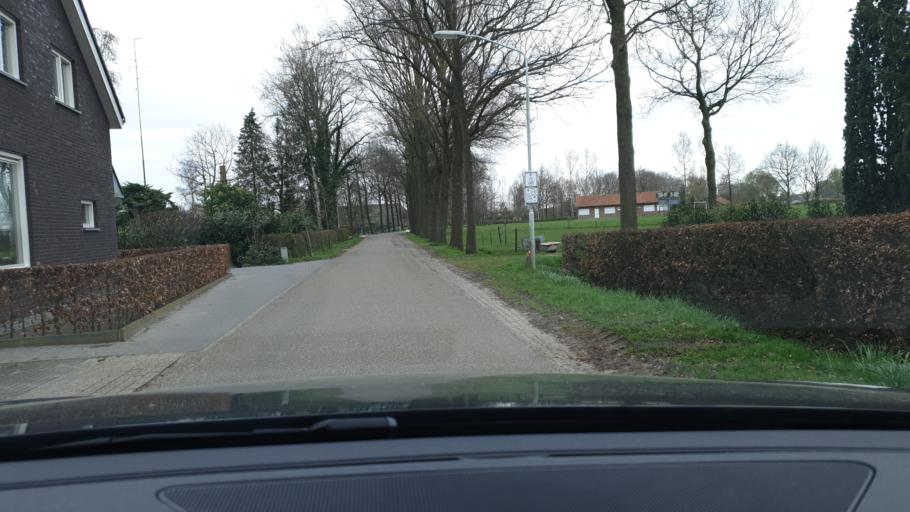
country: NL
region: North Brabant
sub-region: Gemeente Best
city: Best
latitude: 51.5123
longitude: 5.3622
